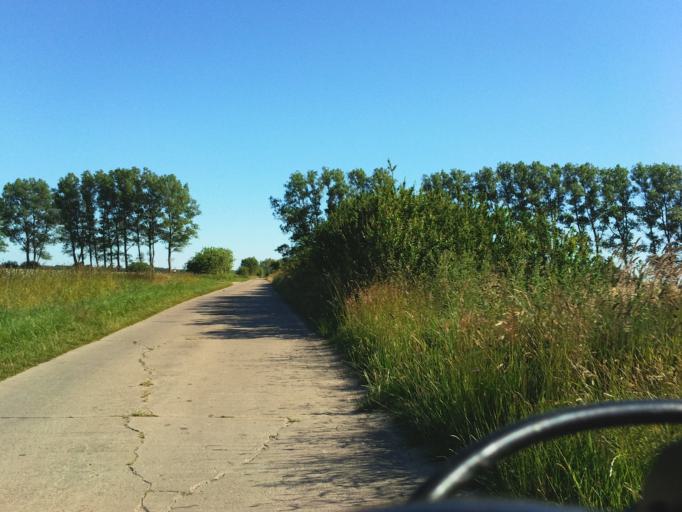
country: DE
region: Mecklenburg-Vorpommern
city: Monchhagen
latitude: 54.1694
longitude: 12.2015
